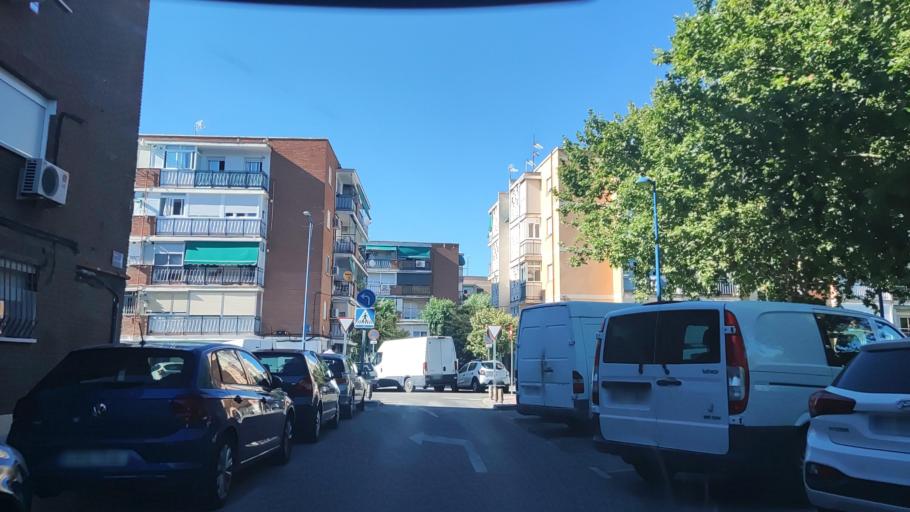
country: ES
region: Madrid
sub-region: Provincia de Madrid
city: Leganes
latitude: 40.3336
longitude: -3.7630
